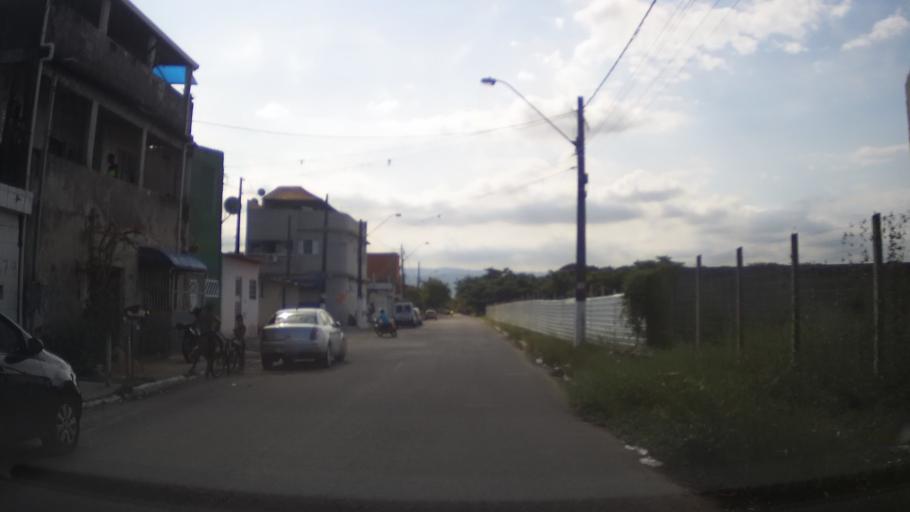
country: BR
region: Sao Paulo
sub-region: Praia Grande
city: Praia Grande
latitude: -23.9999
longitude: -46.4308
